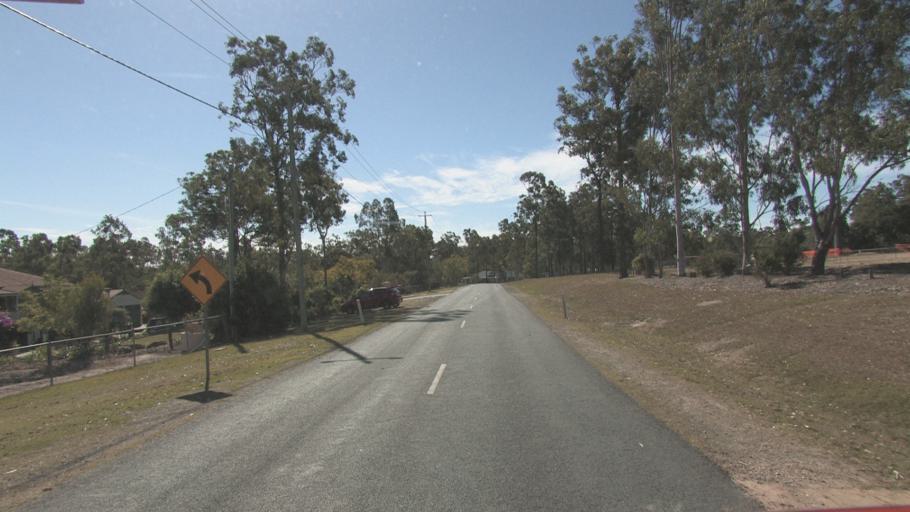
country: AU
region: Queensland
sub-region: Logan
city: North Maclean
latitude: -27.7278
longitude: 152.9619
